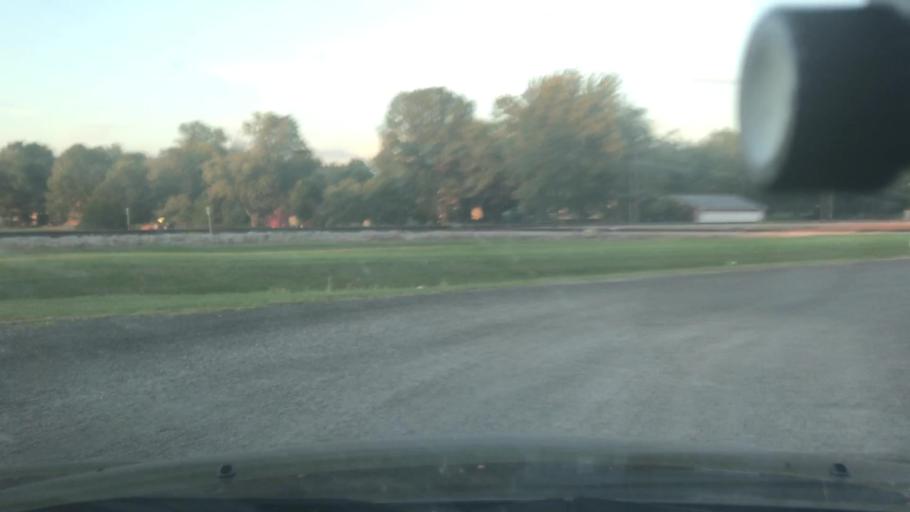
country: US
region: Illinois
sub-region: Washington County
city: Okawville
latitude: 38.3931
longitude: -89.4889
